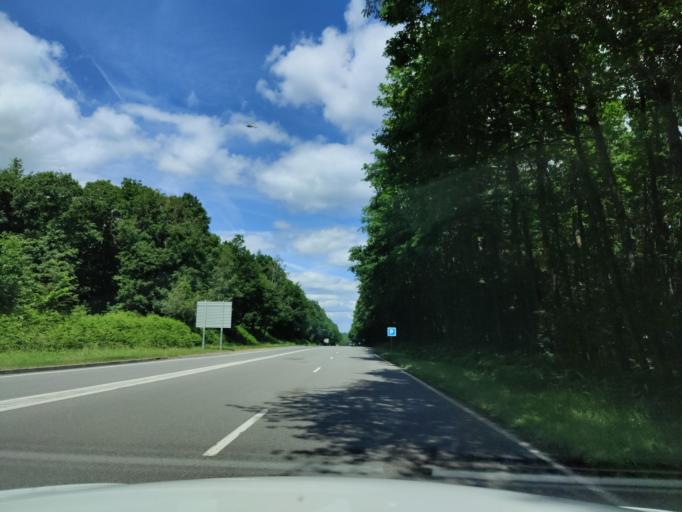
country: FR
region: Centre
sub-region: Departement du Cher
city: Menetou-Salon
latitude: 47.2704
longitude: 2.4277
